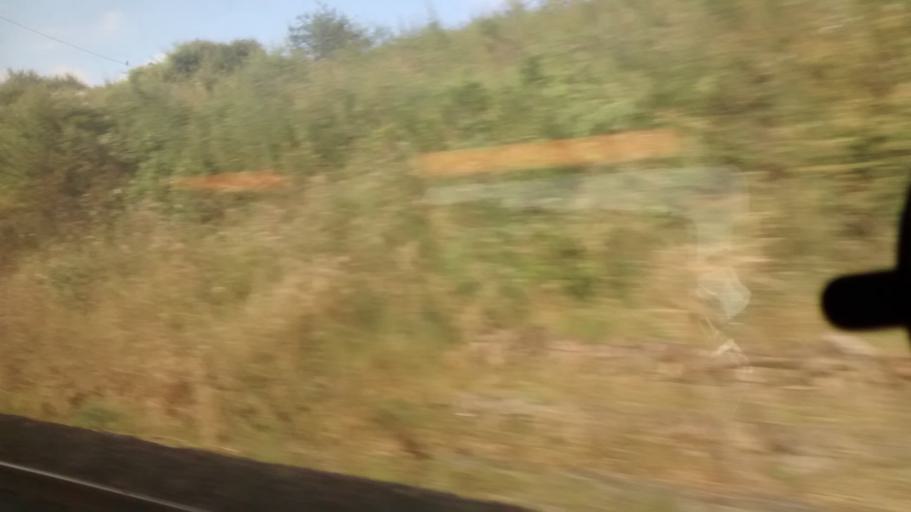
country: FR
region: Pays de la Loire
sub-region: Departement de la Sarthe
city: Saint-Saturnin
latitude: 48.0560
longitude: 0.1604
